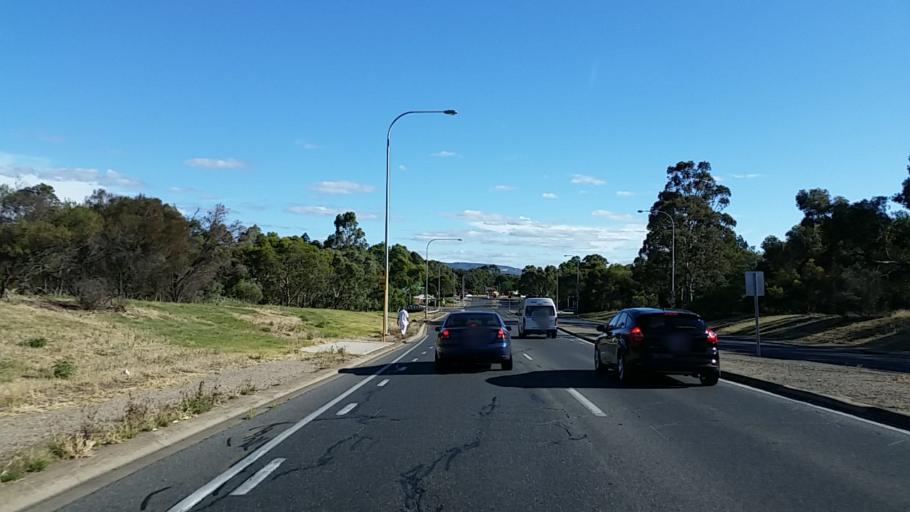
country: AU
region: South Australia
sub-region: Tea Tree Gully
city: Modbury
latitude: -34.8320
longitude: 138.6804
